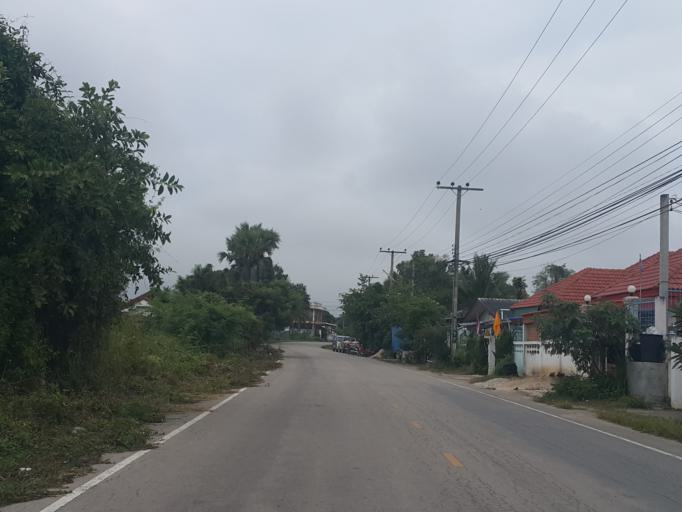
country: TH
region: Lampang
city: Lampang
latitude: 18.3167
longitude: 99.4922
